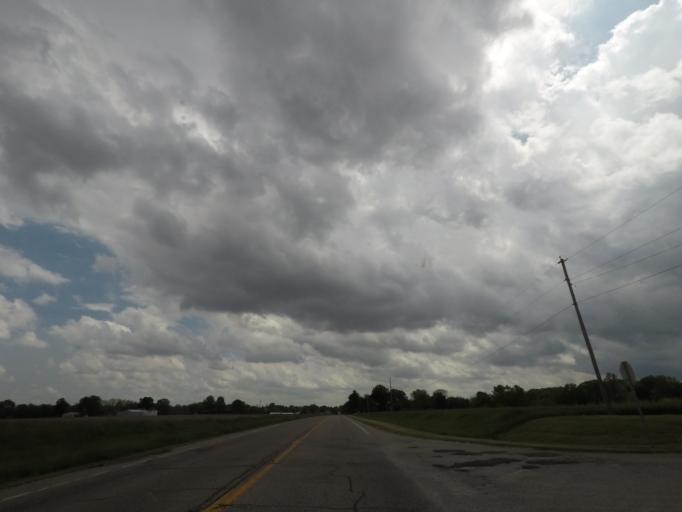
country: US
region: Illinois
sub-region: De Witt County
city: Clinton
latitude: 40.1694
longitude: -88.9605
